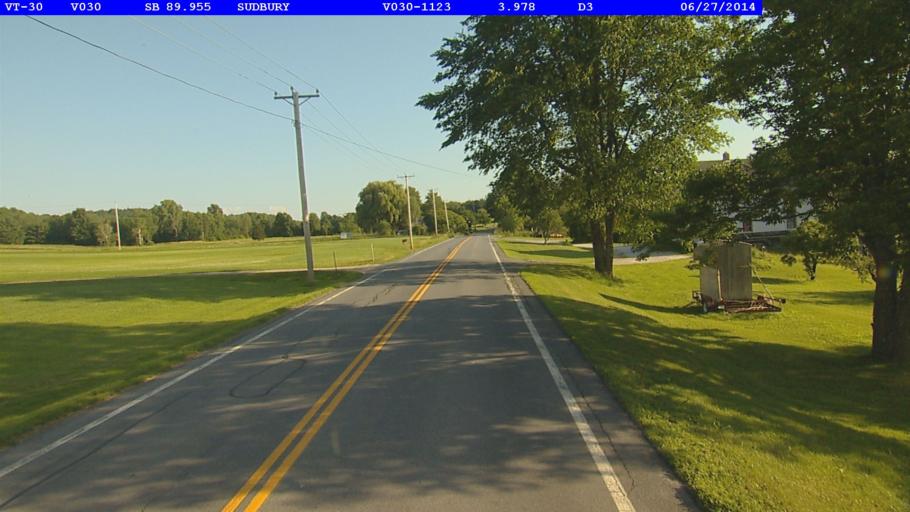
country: US
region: Vermont
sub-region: Rutland County
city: Brandon
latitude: 43.8048
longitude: -73.2019
